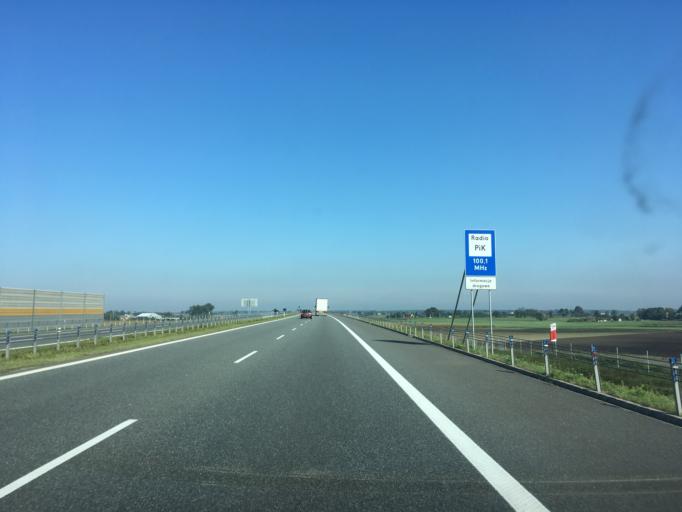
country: PL
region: Kujawsko-Pomorskie
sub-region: Powiat torunski
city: Lubicz Dolny
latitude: 53.1030
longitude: 18.7487
